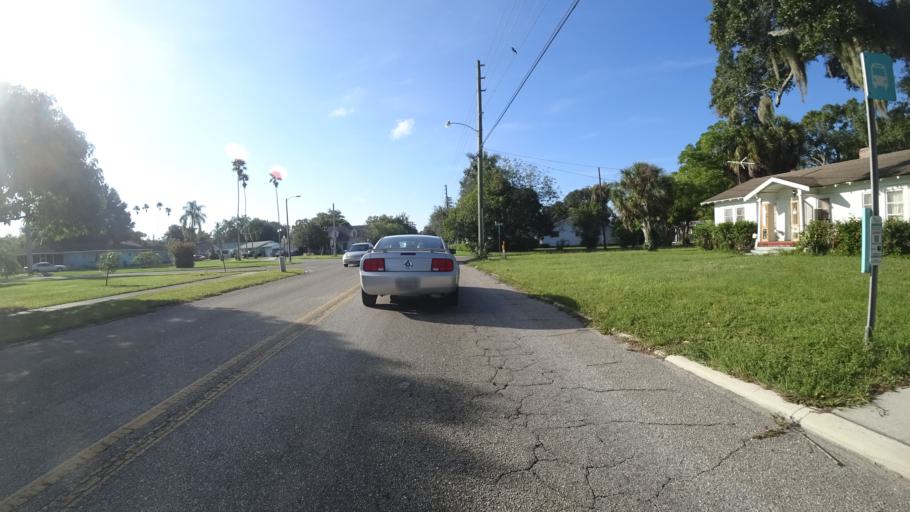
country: US
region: Florida
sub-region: Manatee County
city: Bradenton
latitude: 27.4869
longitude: -82.5876
